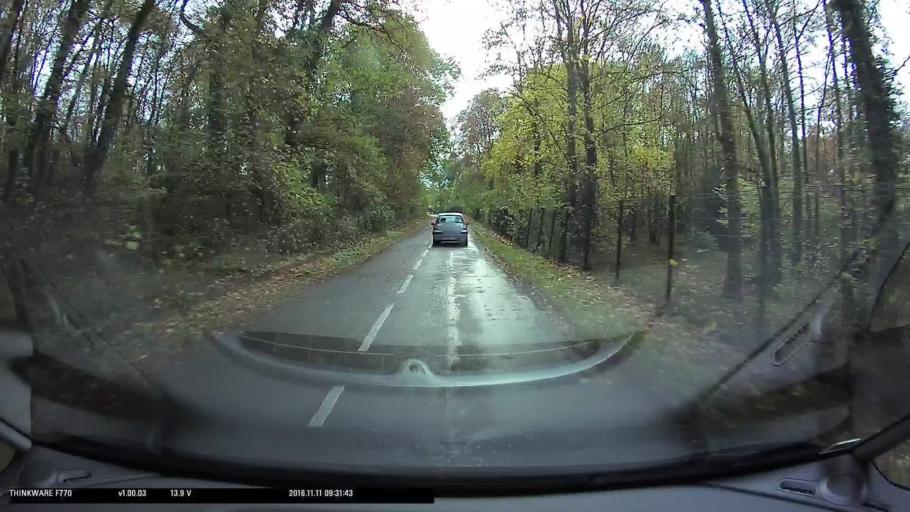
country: FR
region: Ile-de-France
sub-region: Departement du Val-d'Oise
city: Osny
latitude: 49.0663
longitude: 2.0632
